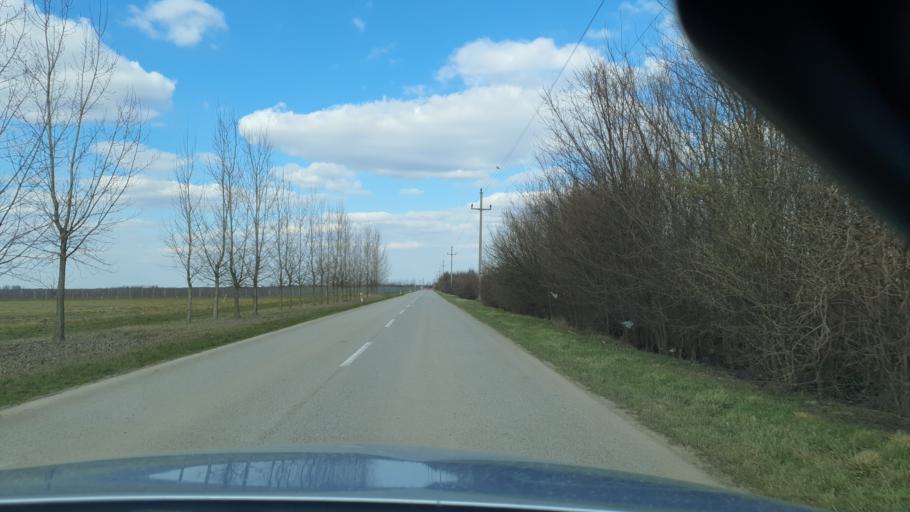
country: RS
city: Kulpin
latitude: 45.4249
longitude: 19.6015
